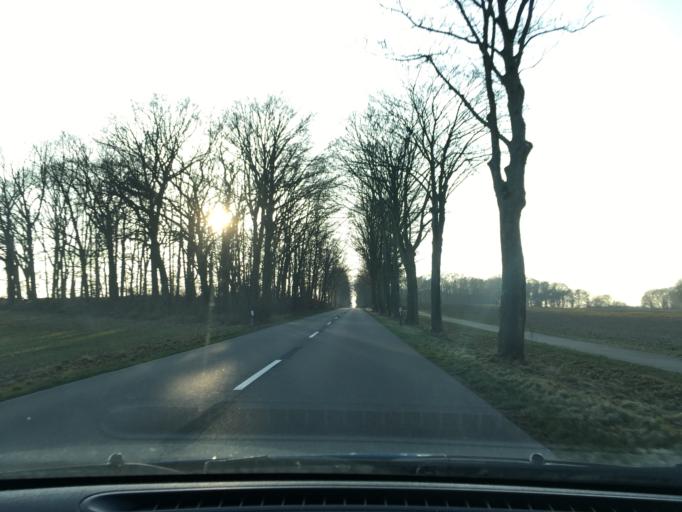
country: DE
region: Lower Saxony
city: Bad Bevensen
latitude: 53.0682
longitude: 10.5479
